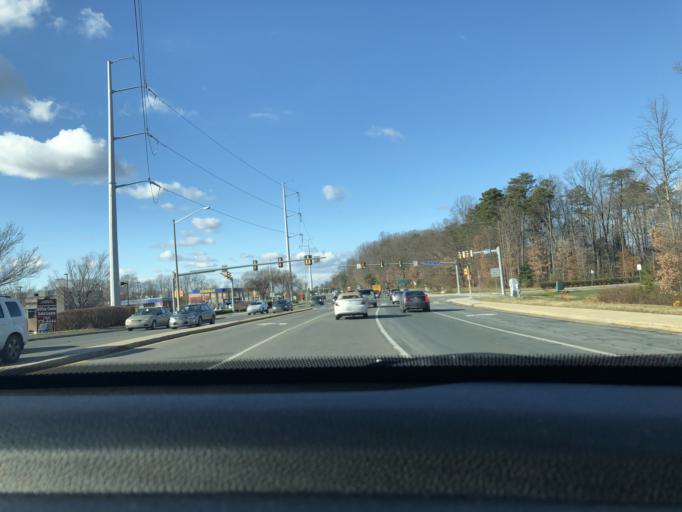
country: US
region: Virginia
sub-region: City of Fairfax
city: Fairfax
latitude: 38.8250
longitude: -77.3117
